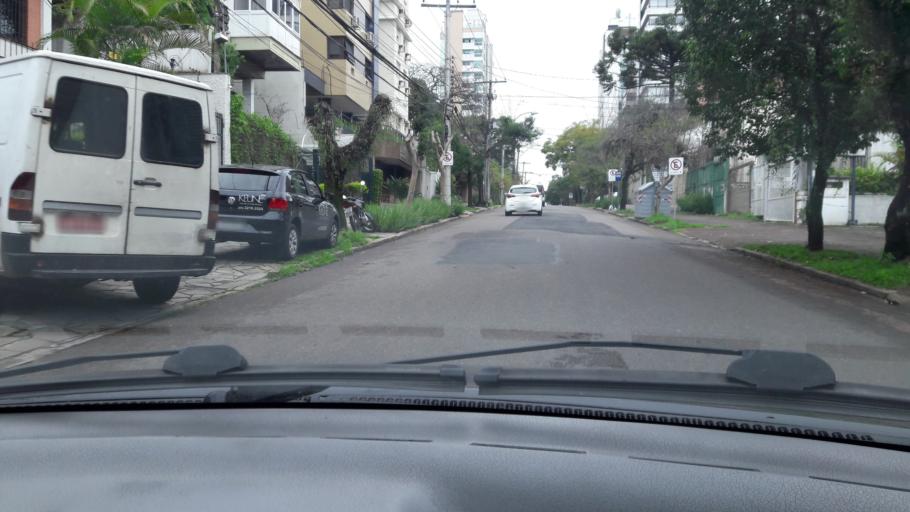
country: BR
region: Rio Grande do Sul
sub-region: Porto Alegre
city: Porto Alegre
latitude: -30.0268
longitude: -51.1854
